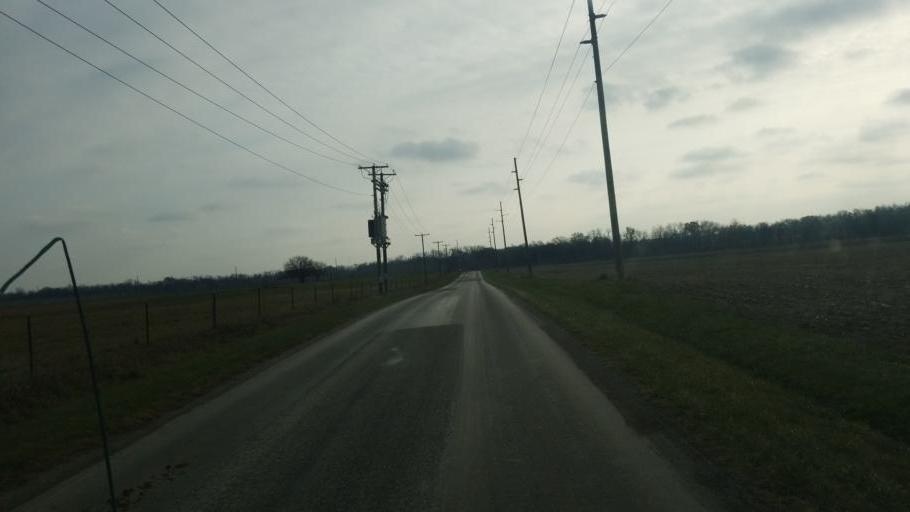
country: US
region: Indiana
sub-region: Adams County
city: Geneva
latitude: 40.6251
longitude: -84.9642
